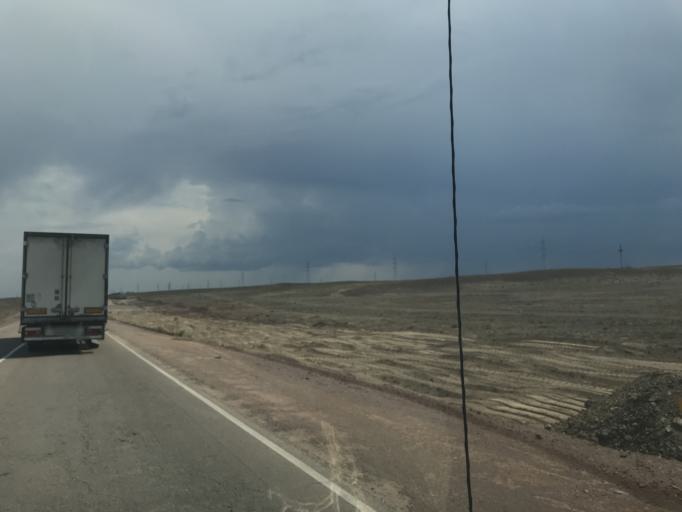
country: KZ
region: Zhambyl
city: Mynaral
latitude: 45.2983
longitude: 73.7660
